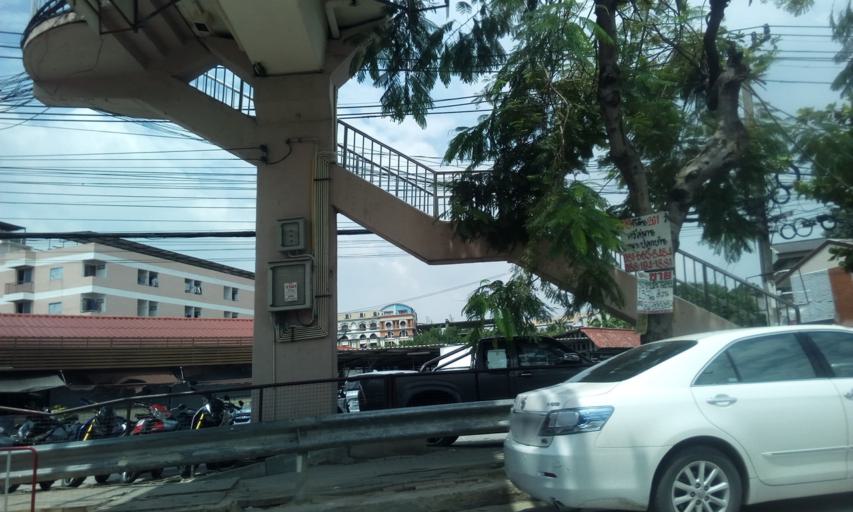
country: TH
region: Bangkok
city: Don Mueang
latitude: 13.9377
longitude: 100.5465
